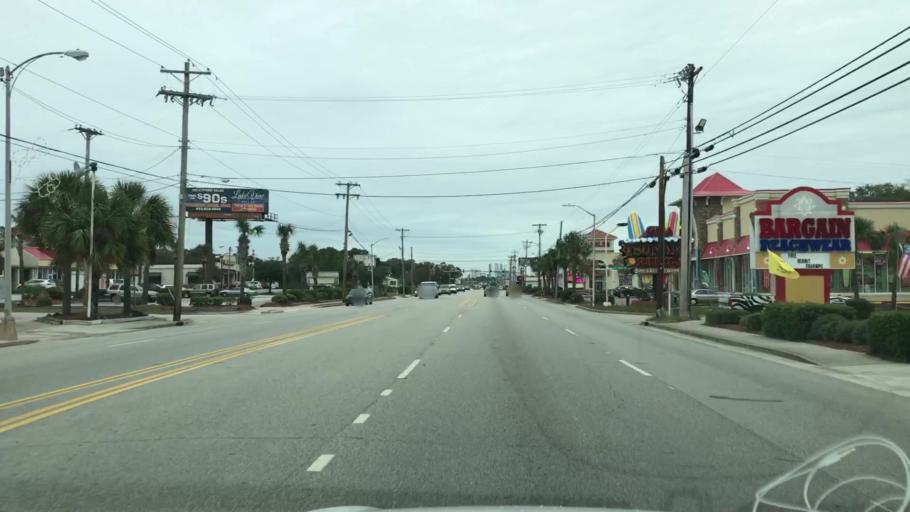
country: US
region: South Carolina
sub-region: Horry County
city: Myrtle Beach
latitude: 33.6784
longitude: -78.9002
